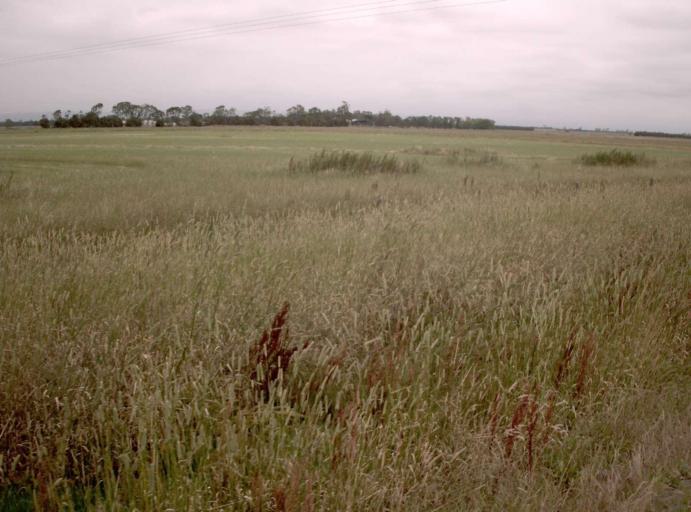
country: AU
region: Victoria
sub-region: Wellington
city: Heyfield
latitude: -38.0992
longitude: 146.7732
